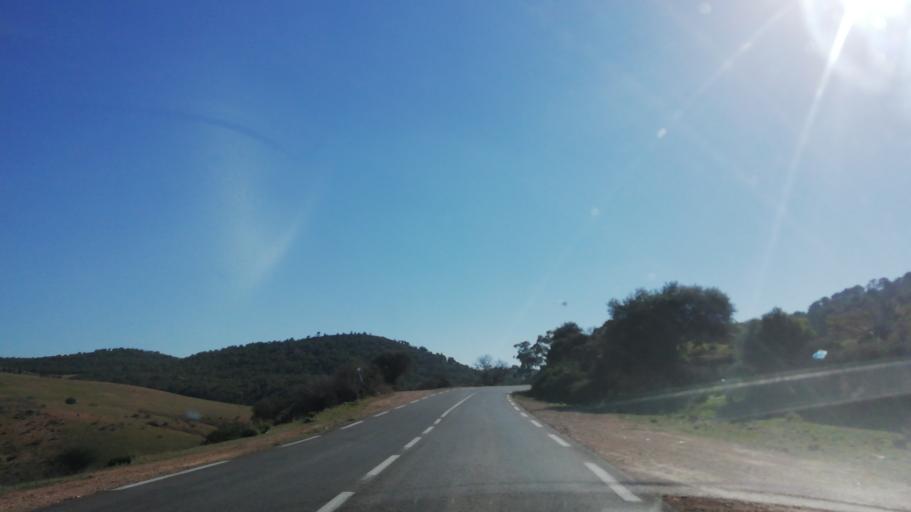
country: DZ
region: Tlemcen
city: Nedroma
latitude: 34.8239
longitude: -1.6381
